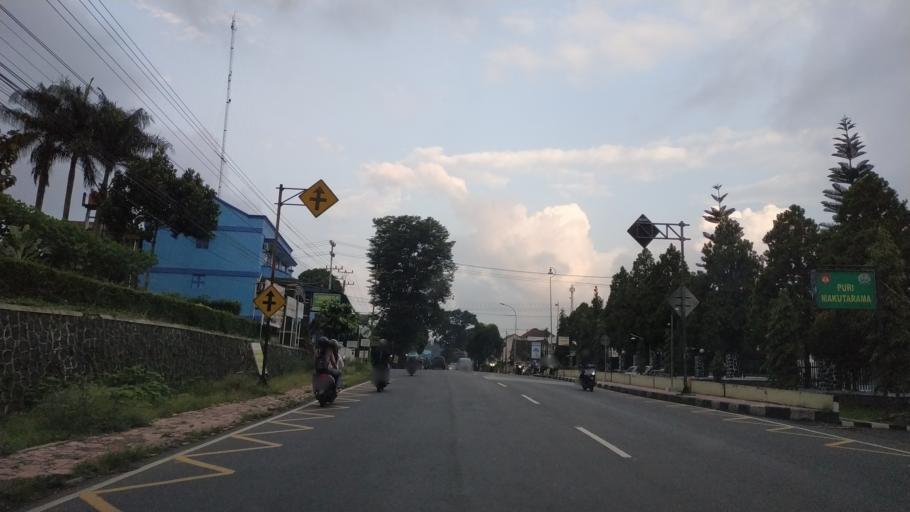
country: ID
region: Central Java
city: Salatiga
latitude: -7.3159
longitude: 110.4942
